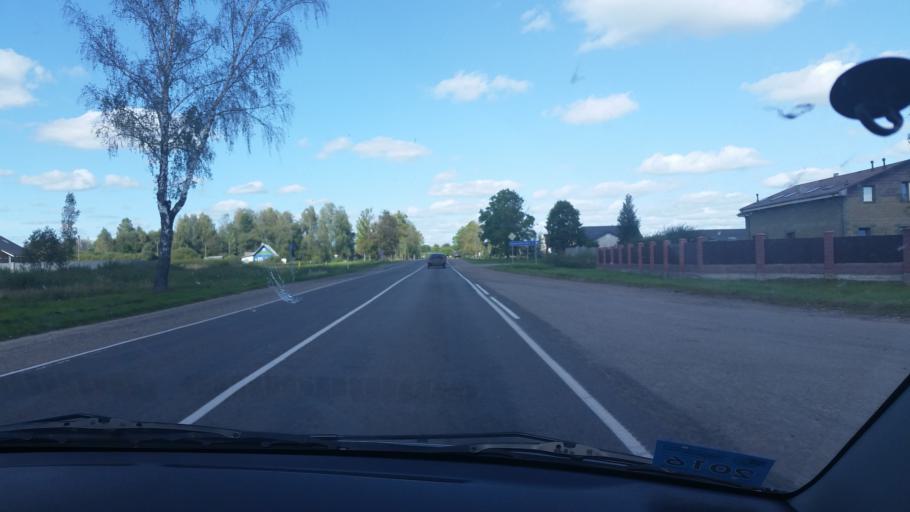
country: BY
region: Vitebsk
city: Vitebsk
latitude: 55.1124
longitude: 30.2827
